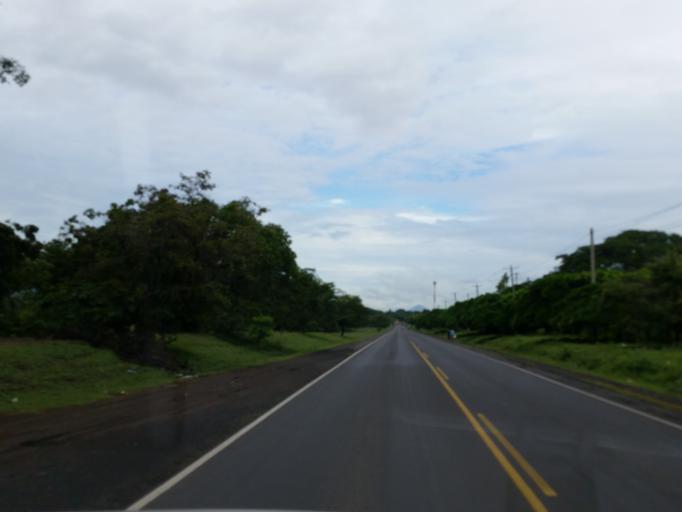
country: NI
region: Managua
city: Ciudad Sandino
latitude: 12.2278
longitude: -86.4137
